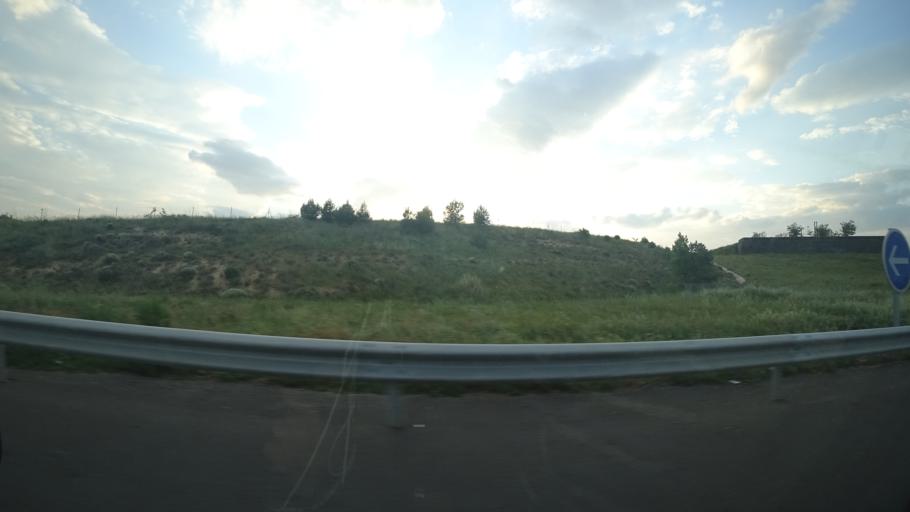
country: FR
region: Languedoc-Roussillon
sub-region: Departement de l'Herault
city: Paulhan
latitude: 43.5411
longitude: 3.4446
